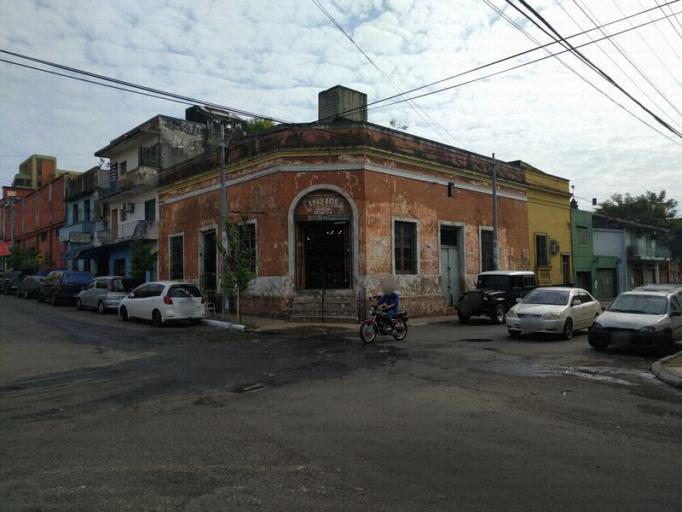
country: PY
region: Asuncion
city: Asuncion
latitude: -25.2784
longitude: -57.6443
